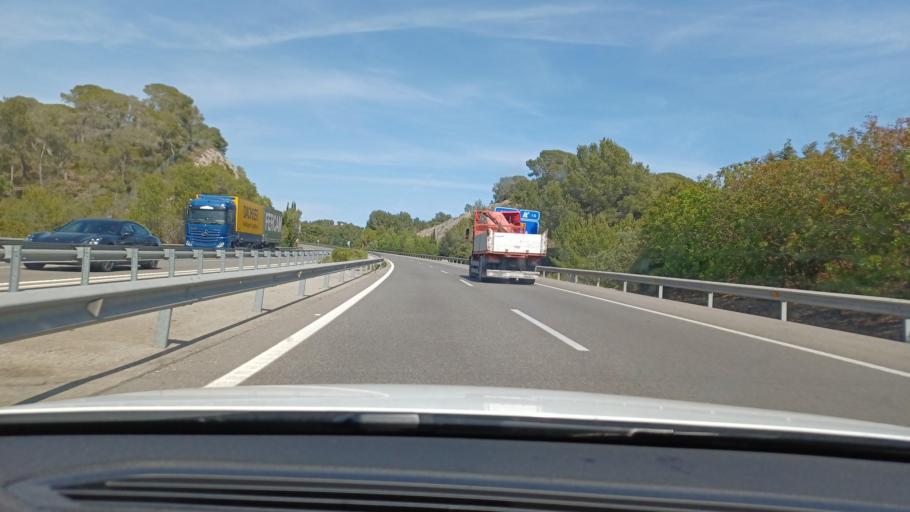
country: ES
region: Catalonia
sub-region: Provincia de Barcelona
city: Cubelles
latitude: 41.2142
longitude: 1.6683
